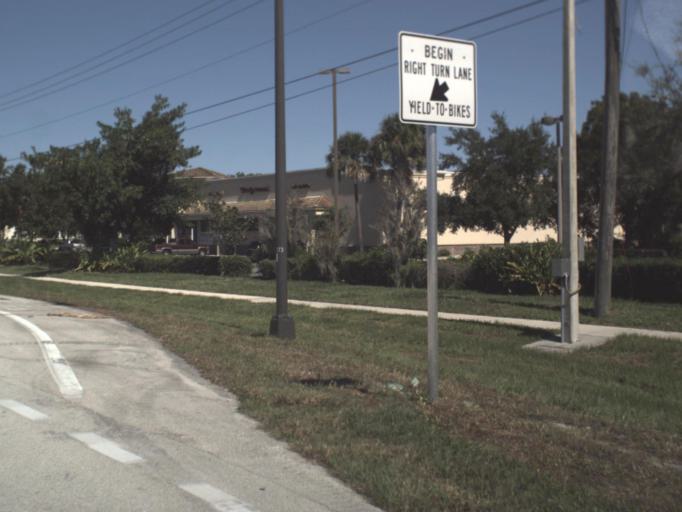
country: US
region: Florida
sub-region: Lee County
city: Bonita Springs
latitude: 26.3729
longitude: -81.8077
